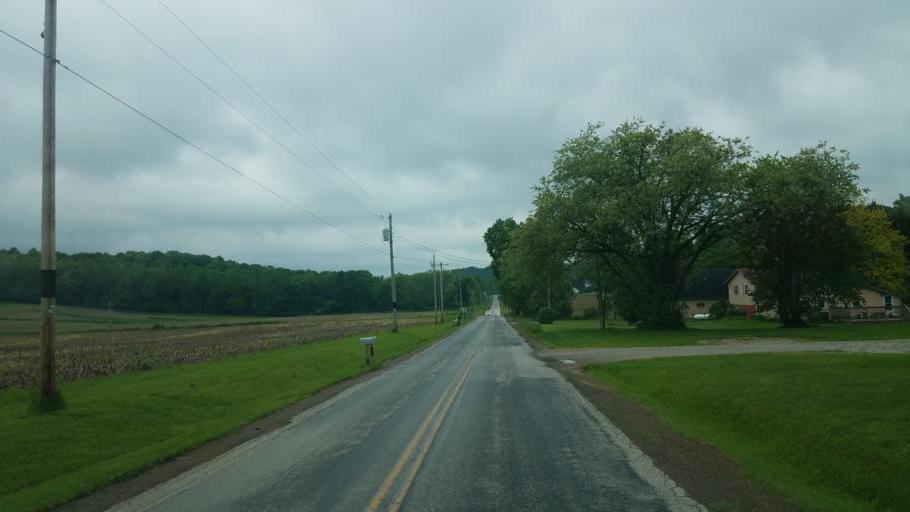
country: US
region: Ohio
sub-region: Richland County
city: Lincoln Heights
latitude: 40.7506
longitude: -82.3877
